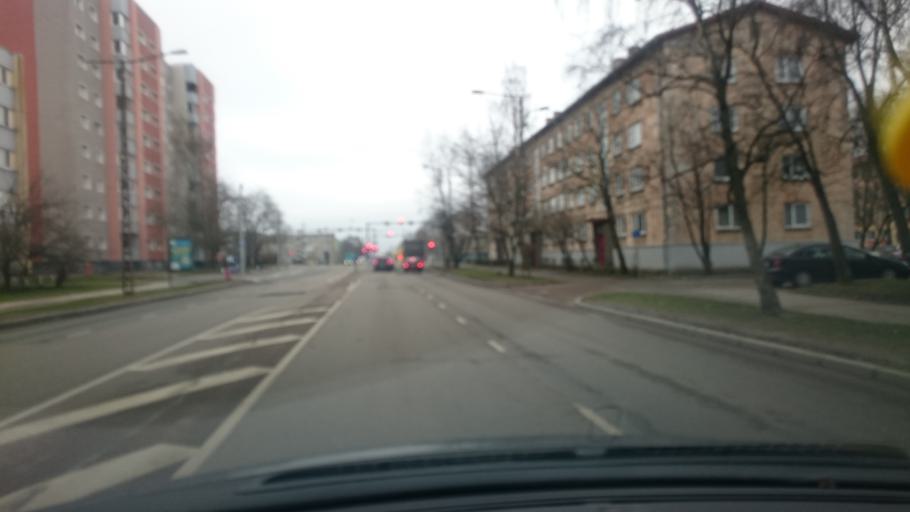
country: EE
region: Harju
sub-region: Tallinna linn
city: Tallinn
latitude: 59.4476
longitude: 24.6996
